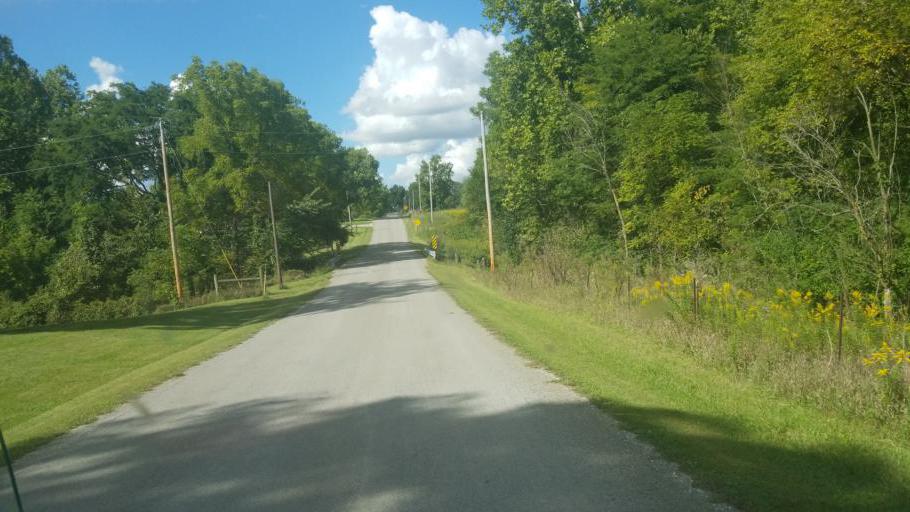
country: US
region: Ohio
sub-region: Hardin County
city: Kenton
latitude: 40.5401
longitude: -83.5434
